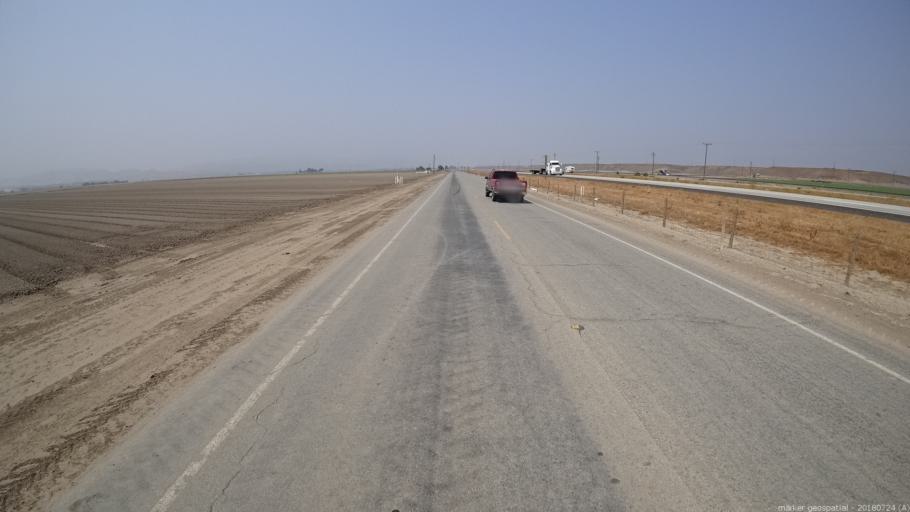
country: US
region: California
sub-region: Monterey County
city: King City
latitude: 36.1917
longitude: -121.0831
